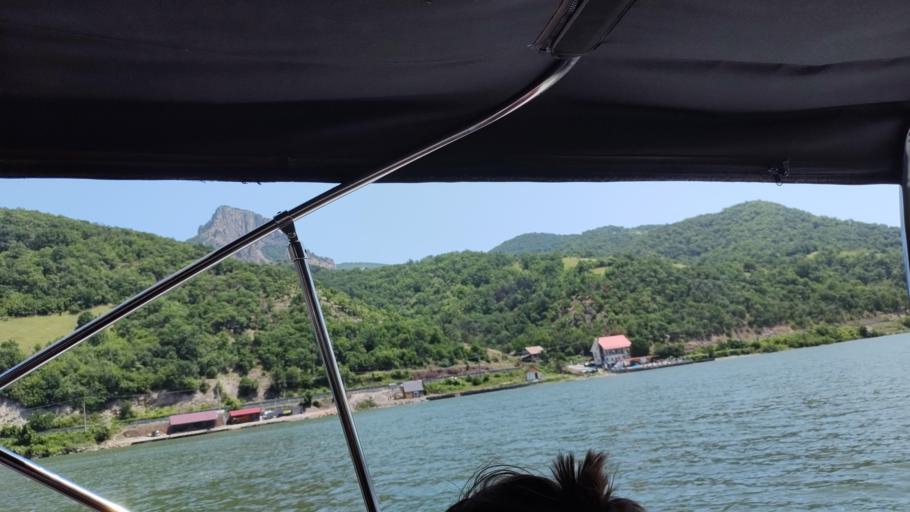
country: RO
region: Mehedinti
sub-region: Comuna Svinita
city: Svinita
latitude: 44.5607
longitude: 22.0307
